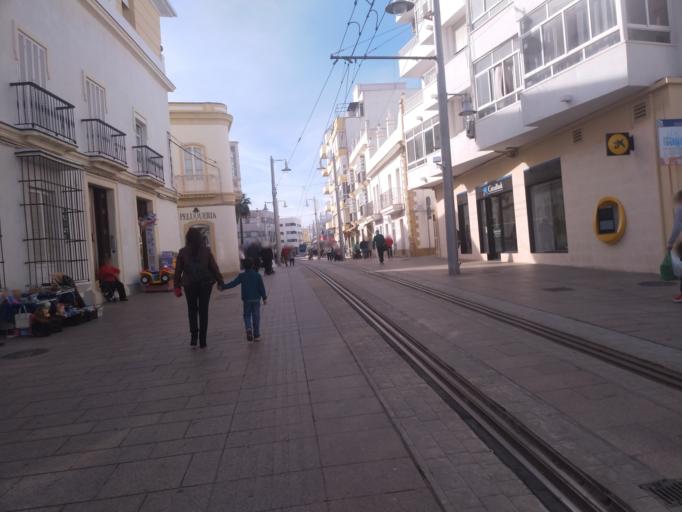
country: ES
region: Andalusia
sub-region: Provincia de Cadiz
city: San Fernando
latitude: 36.4588
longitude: -6.2026
